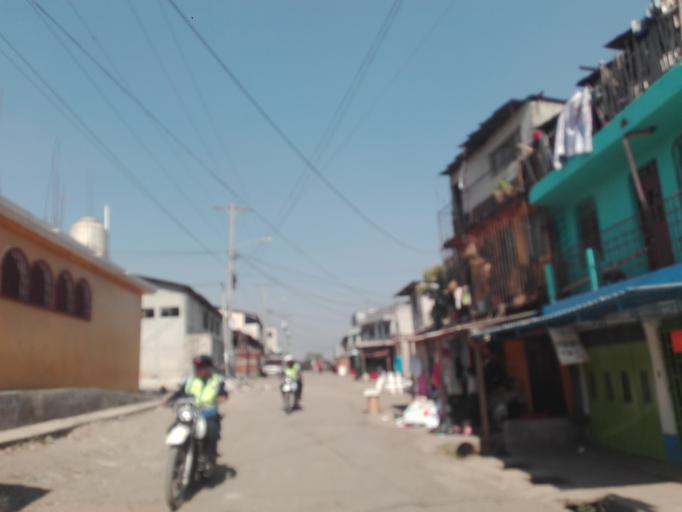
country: GT
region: Guatemala
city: Villa Nueva
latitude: 14.5073
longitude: -90.5954
